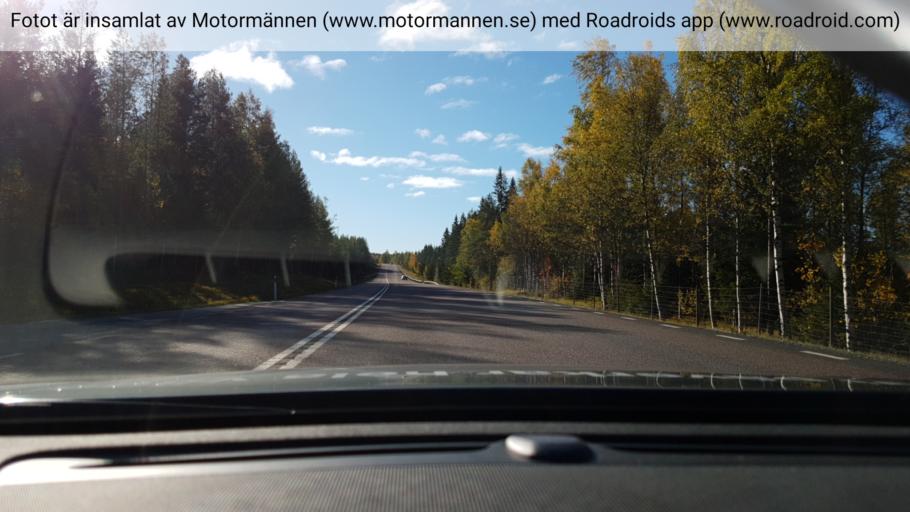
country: SE
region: Vaesterbotten
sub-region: Skelleftea Kommun
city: Burea
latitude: 64.4513
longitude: 21.2842
